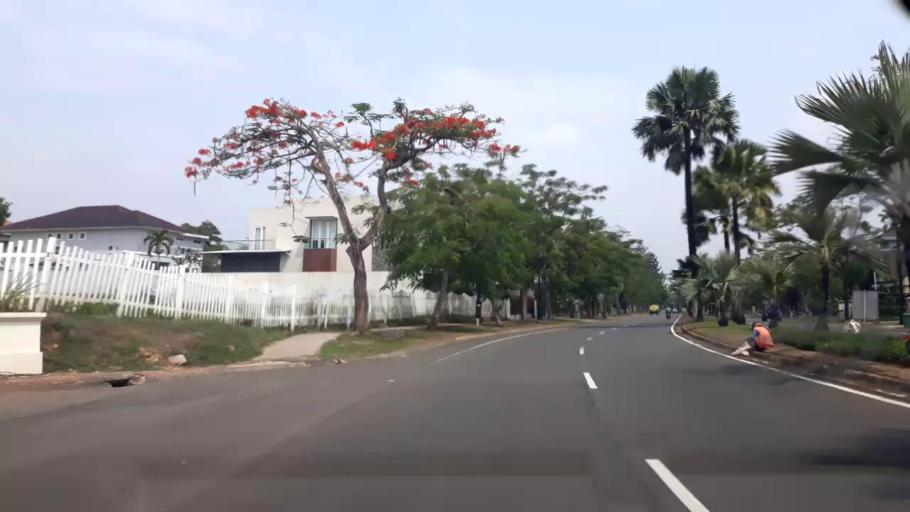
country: ID
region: Banten
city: Curug
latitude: -6.2407
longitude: 106.5976
